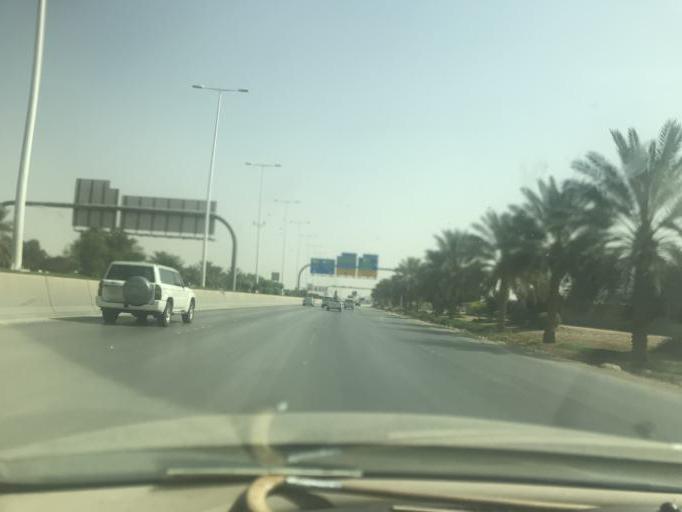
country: SA
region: Ar Riyad
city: Riyadh
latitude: 24.7321
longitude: 46.7090
